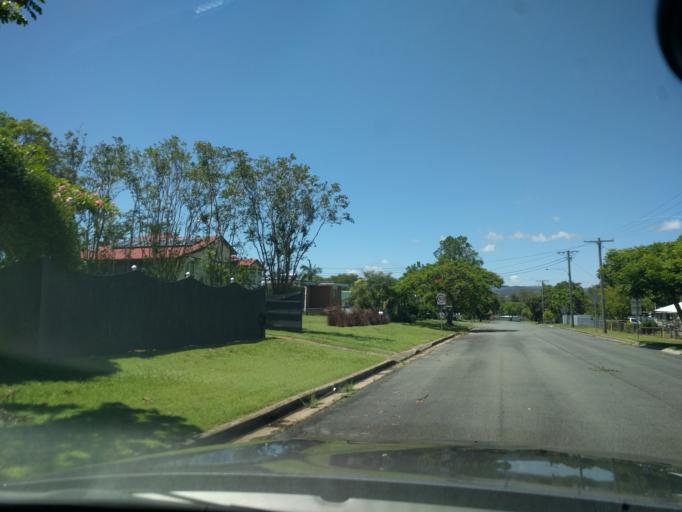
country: AU
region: Queensland
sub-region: Logan
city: Cedar Vale
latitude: -27.9896
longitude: 153.0044
